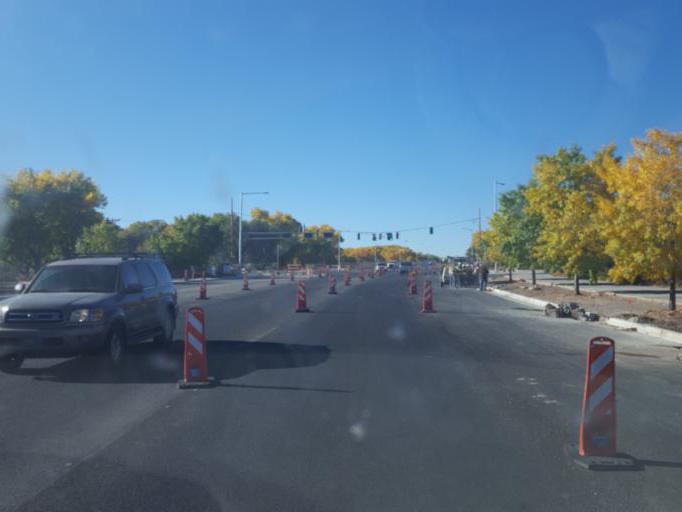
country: US
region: New Mexico
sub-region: Bernalillo County
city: Albuquerque
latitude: 35.0924
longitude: -106.6785
